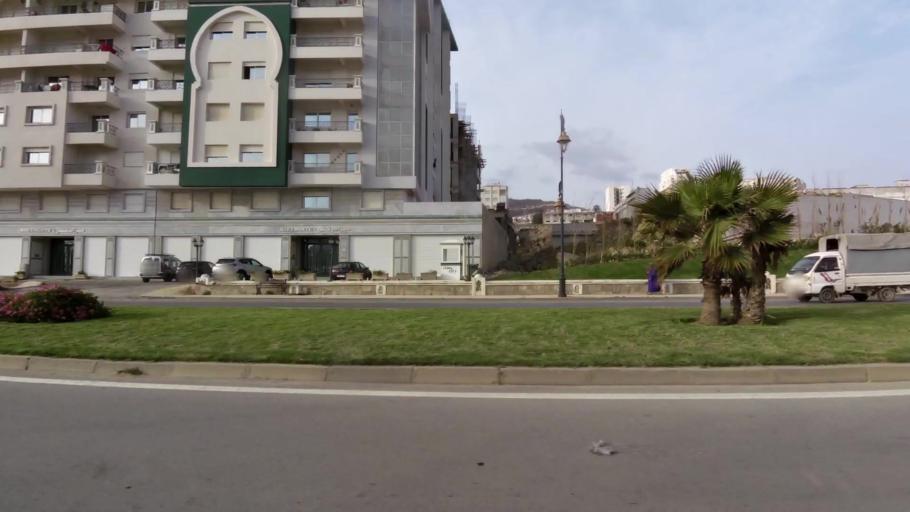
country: MA
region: Tanger-Tetouan
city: Tetouan
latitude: 35.5662
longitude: -5.3846
